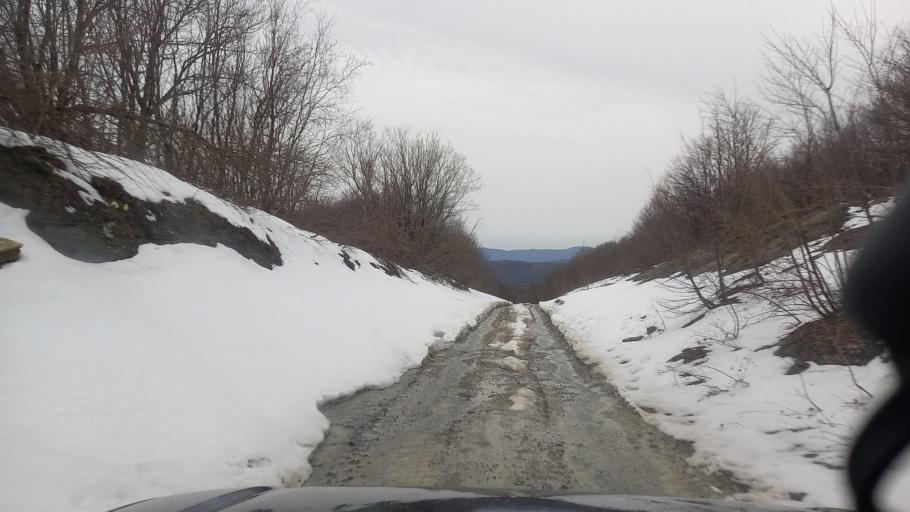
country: RU
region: Krasnodarskiy
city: Pshada
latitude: 44.5930
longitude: 38.3102
